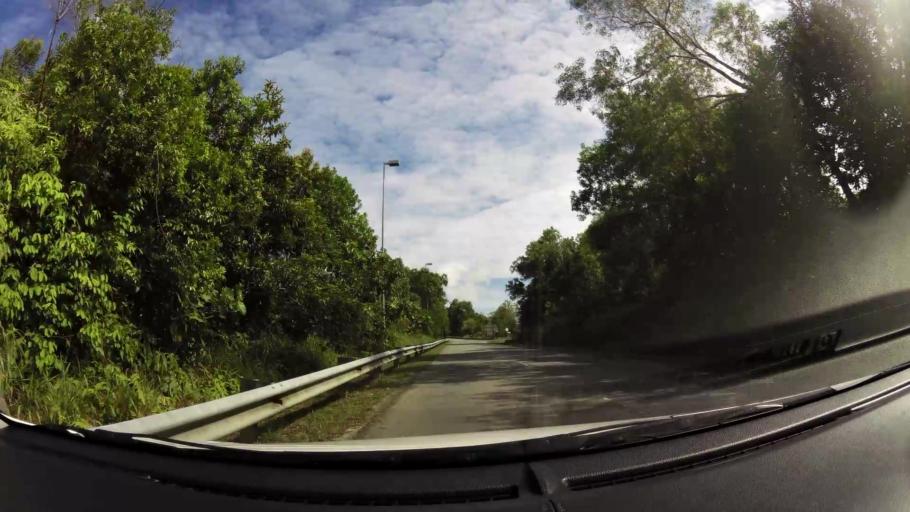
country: BN
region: Brunei and Muara
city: Bandar Seri Begawan
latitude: 4.9283
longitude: 114.9058
